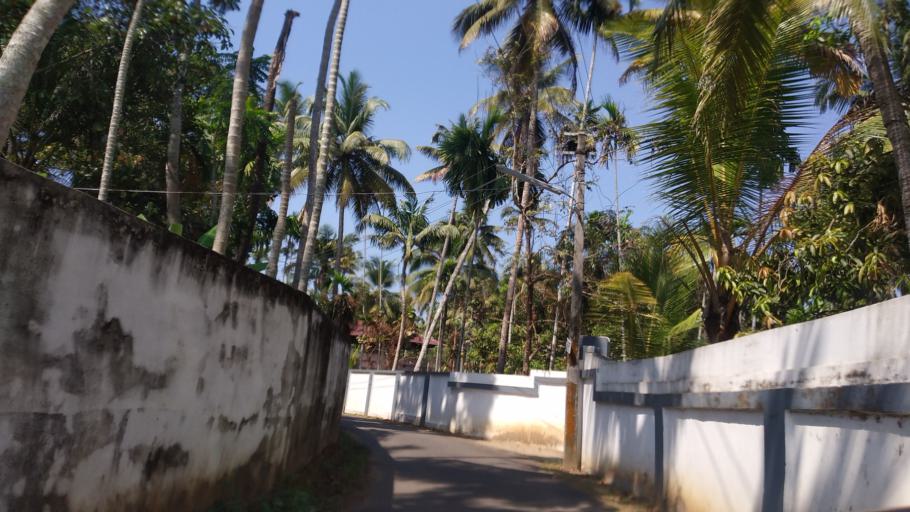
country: IN
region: Kerala
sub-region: Thrissur District
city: Kodungallur
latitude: 10.1420
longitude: 76.1950
